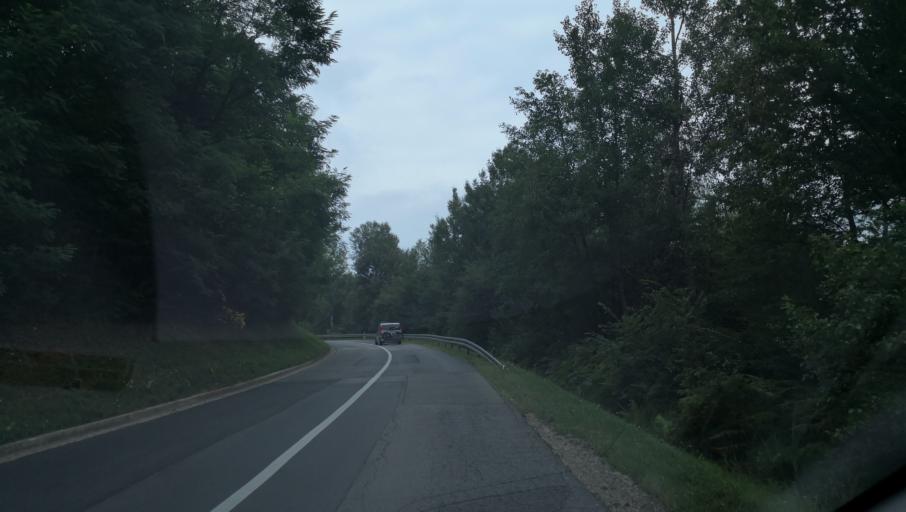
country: HR
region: Karlovacka
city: Ozalj
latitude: 45.5211
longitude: 15.3937
